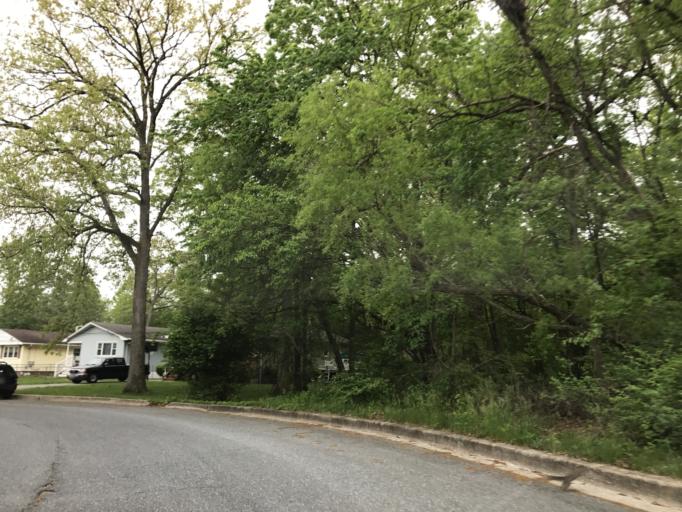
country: US
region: Maryland
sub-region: Baltimore County
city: Essex
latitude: 39.3167
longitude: -76.4542
